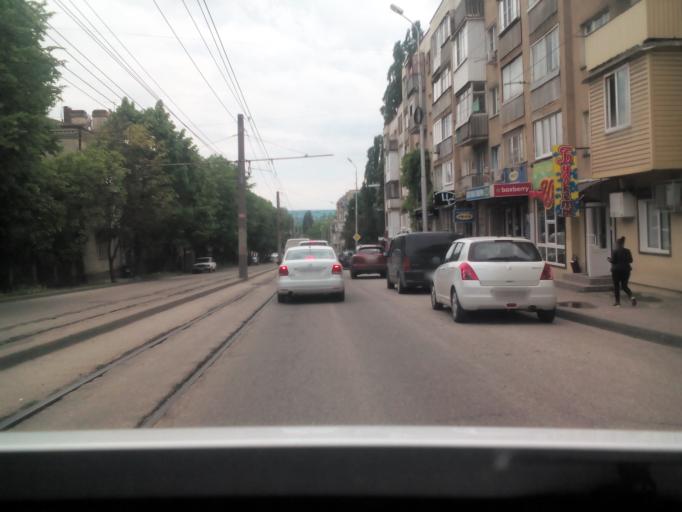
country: RU
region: Stavropol'skiy
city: Pyatigorsk
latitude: 44.0484
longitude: 43.0633
